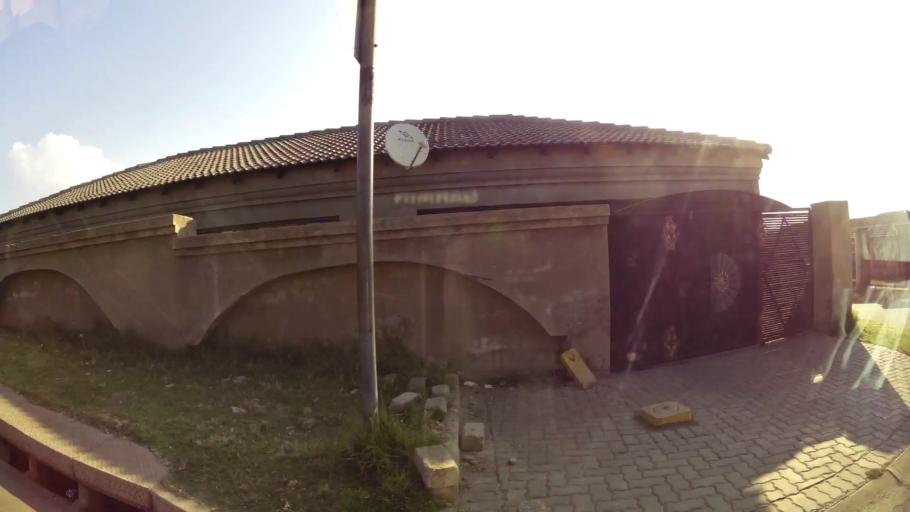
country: ZA
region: Gauteng
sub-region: Ekurhuleni Metropolitan Municipality
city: Tembisa
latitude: -25.9504
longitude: 28.2094
